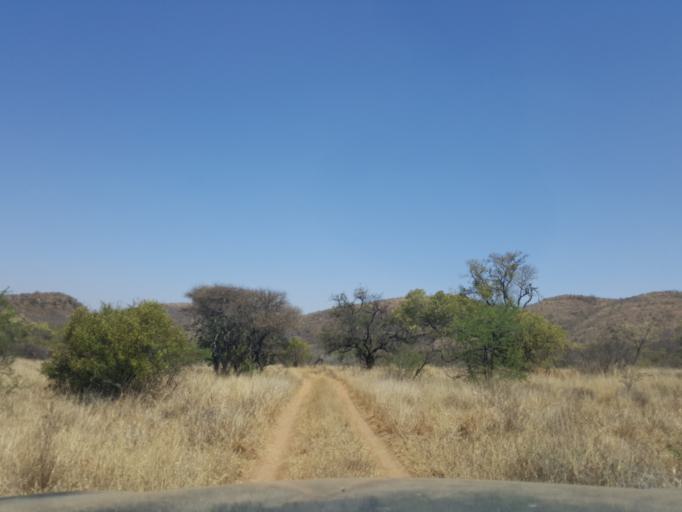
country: BW
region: South East
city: Lobatse
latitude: -25.1391
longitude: 25.6715
